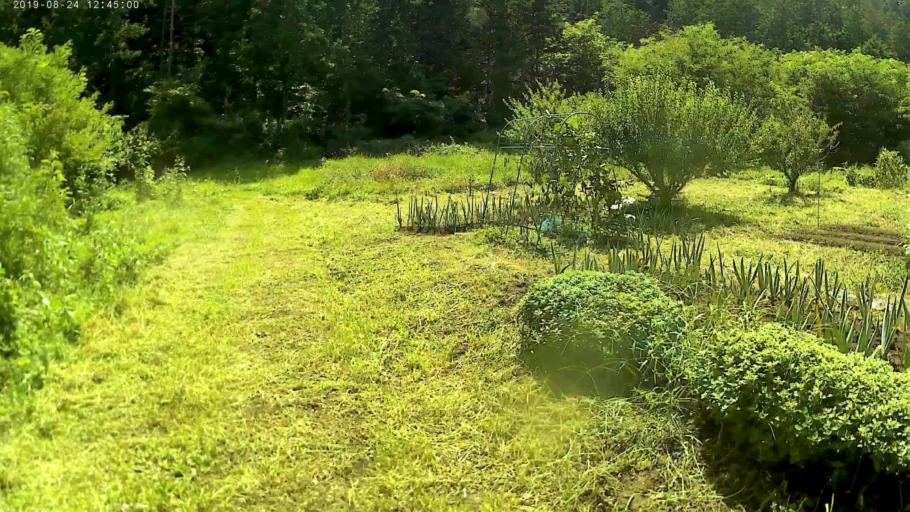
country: JP
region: Nagano
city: Komoro
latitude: 36.2662
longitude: 138.3708
